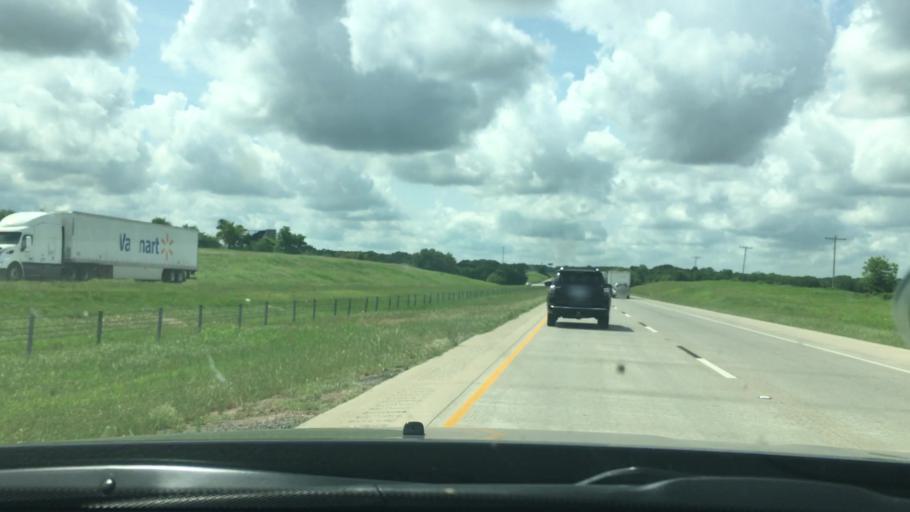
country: US
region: Oklahoma
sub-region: Love County
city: Marietta
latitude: 33.8627
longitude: -97.1343
